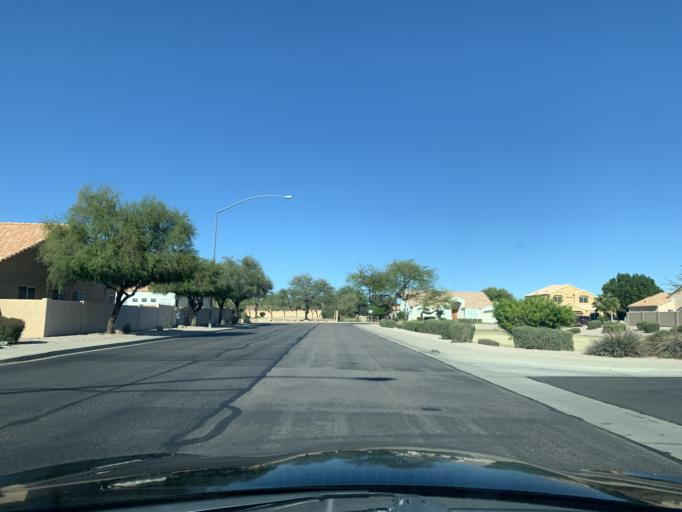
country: US
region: Arizona
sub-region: Pinal County
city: Apache Junction
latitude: 33.3841
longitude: -111.6242
